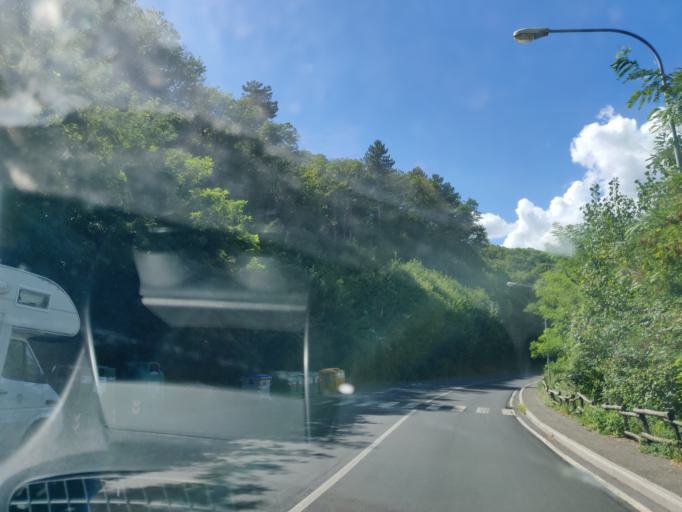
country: IT
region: Tuscany
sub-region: Provincia di Siena
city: Abbadia San Salvatore
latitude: 42.8863
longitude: 11.6690
